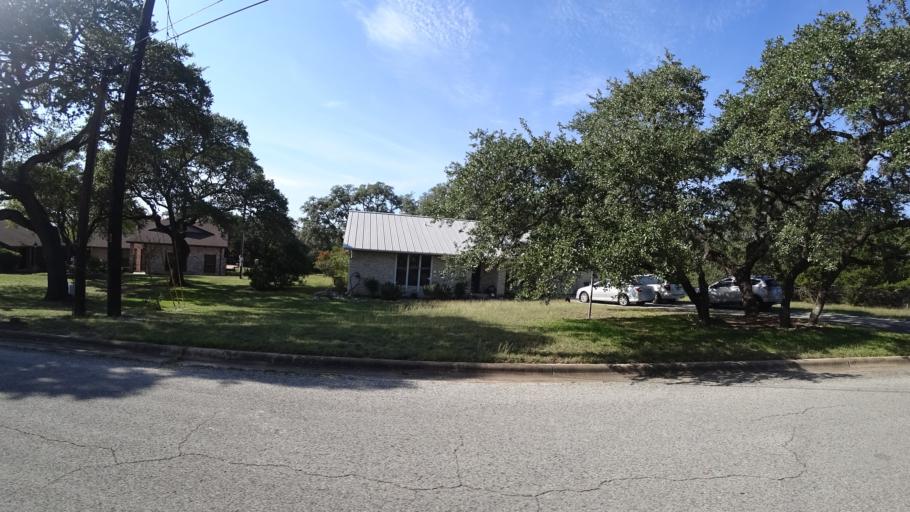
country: US
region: Texas
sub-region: Travis County
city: Shady Hollow
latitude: 30.2183
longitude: -97.9088
